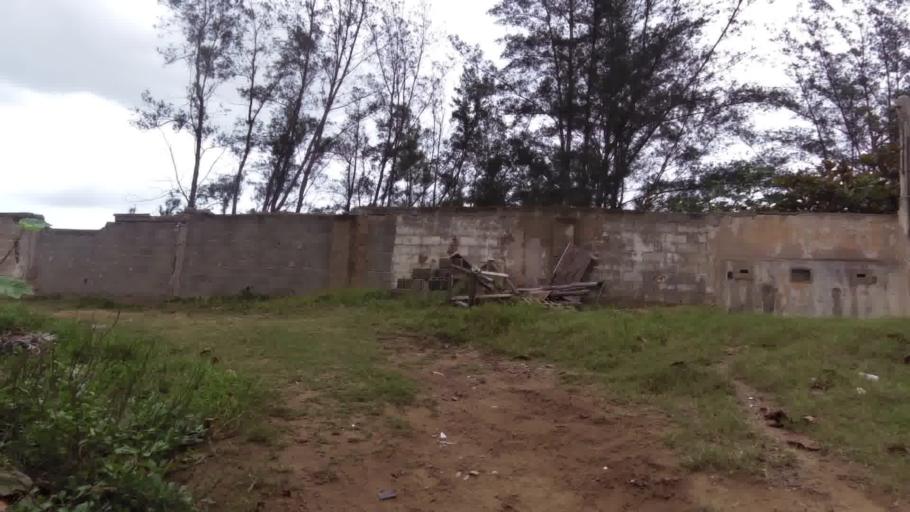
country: BR
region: Espirito Santo
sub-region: Marataizes
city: Marataizes
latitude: -21.0719
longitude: -40.8377
